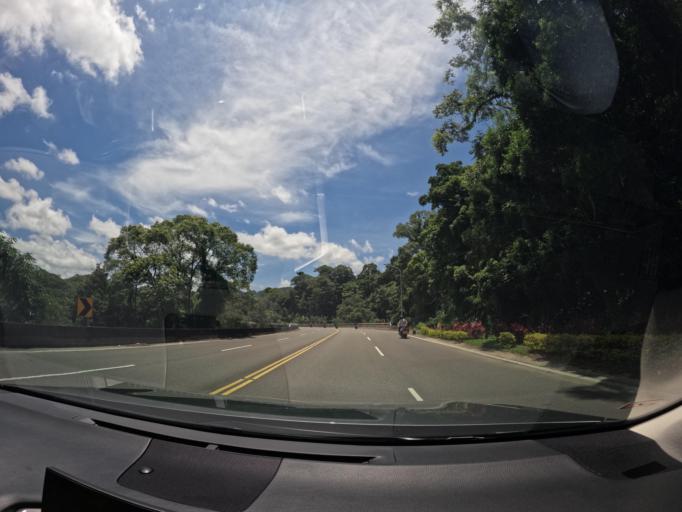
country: TW
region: Taiwan
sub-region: Miaoli
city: Miaoli
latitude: 24.6183
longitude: 120.9459
